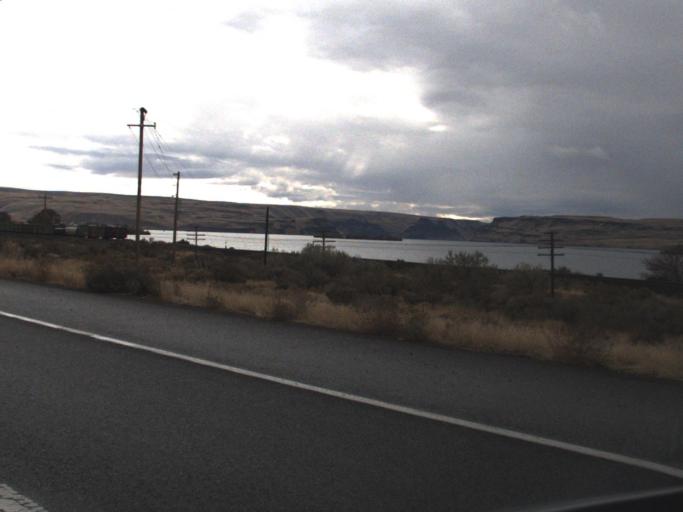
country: US
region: Washington
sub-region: Benton County
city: Finley
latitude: 46.1174
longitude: -118.9254
